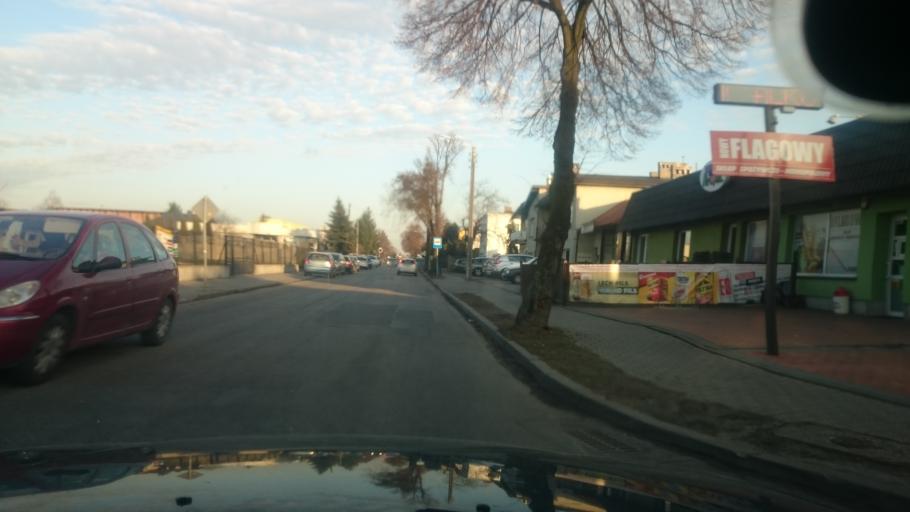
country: PL
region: Greater Poland Voivodeship
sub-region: Powiat ostrowski
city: Ostrow Wielkopolski
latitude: 51.6474
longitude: 17.8281
